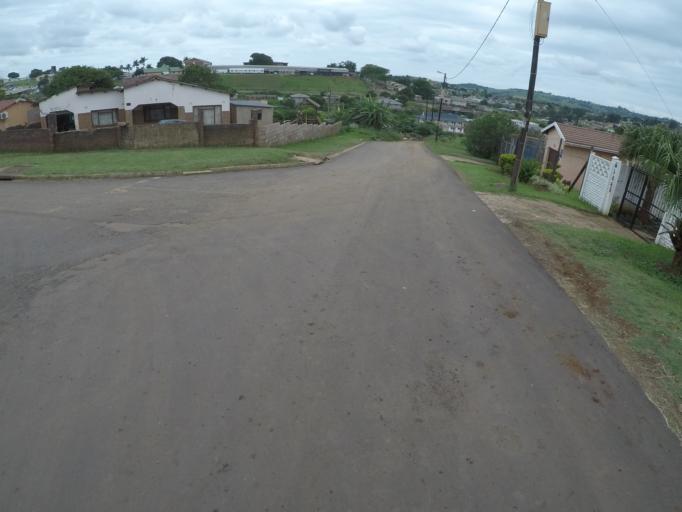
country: ZA
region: KwaZulu-Natal
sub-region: uThungulu District Municipality
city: Empangeni
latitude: -28.7782
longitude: 31.8613
